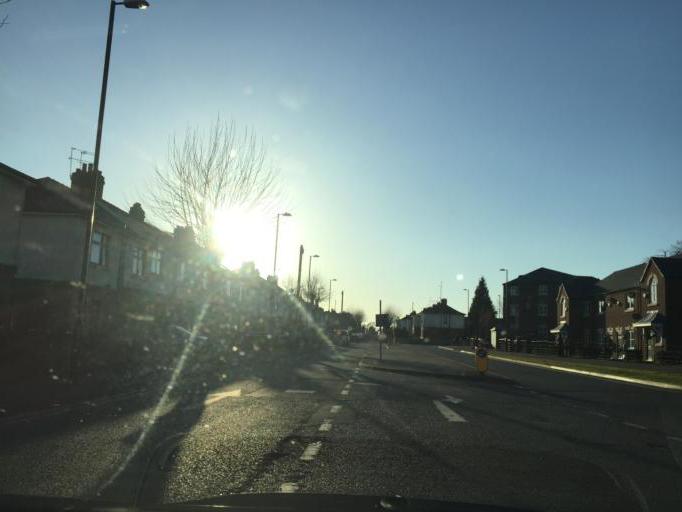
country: GB
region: England
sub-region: Warwickshire
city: Ryton on Dunsmore
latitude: 52.4012
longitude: -1.4644
